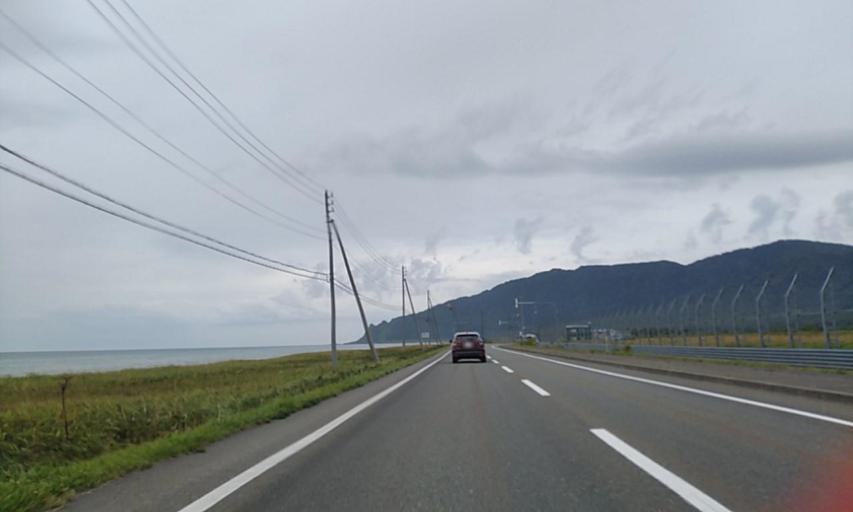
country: JP
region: Hokkaido
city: Makubetsu
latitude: 45.0822
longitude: 142.4562
